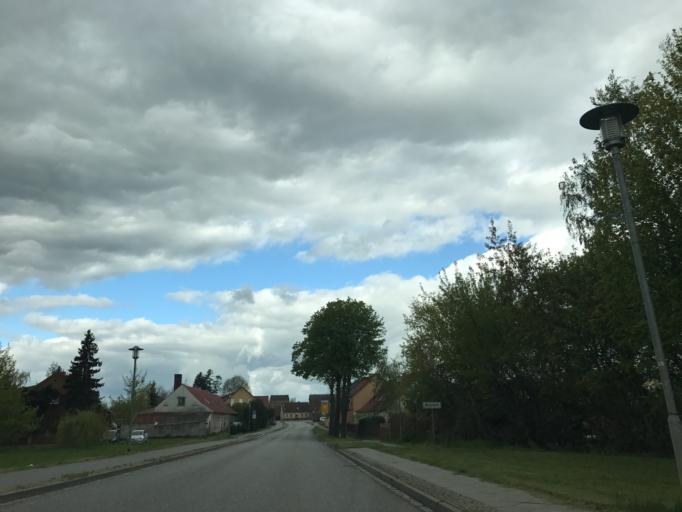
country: DE
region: Brandenburg
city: Wustermark
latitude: 52.5443
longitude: 12.9483
